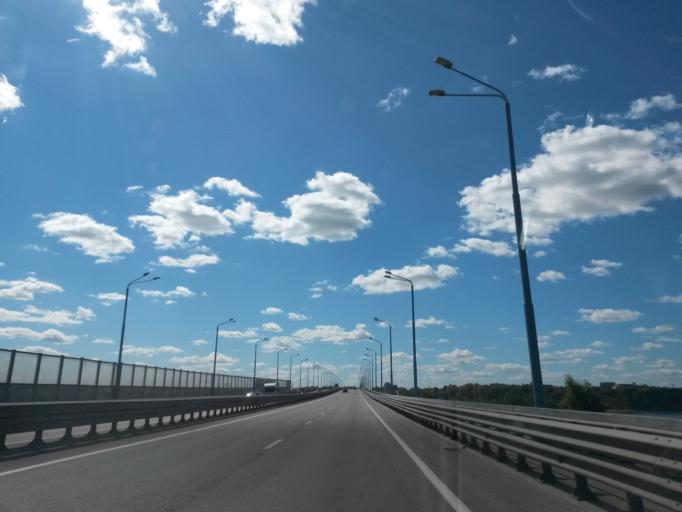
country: RU
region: Jaroslavl
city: Yaroslavl
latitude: 57.6769
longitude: 39.8624
